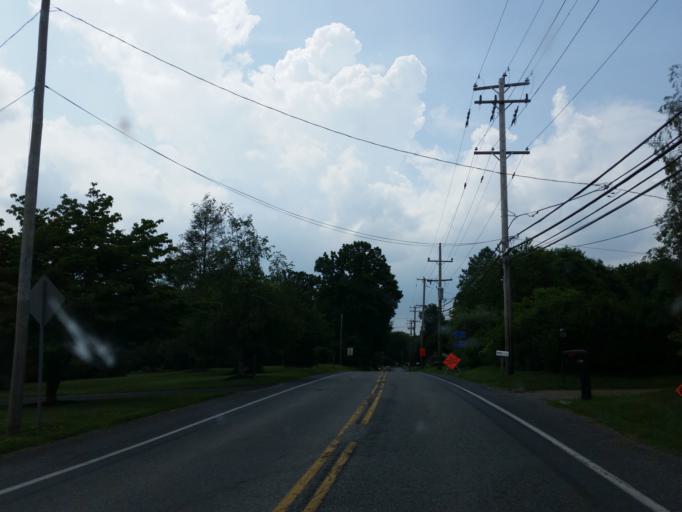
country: US
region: Pennsylvania
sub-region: Chester County
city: West Grove
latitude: 39.7718
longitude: -75.8571
